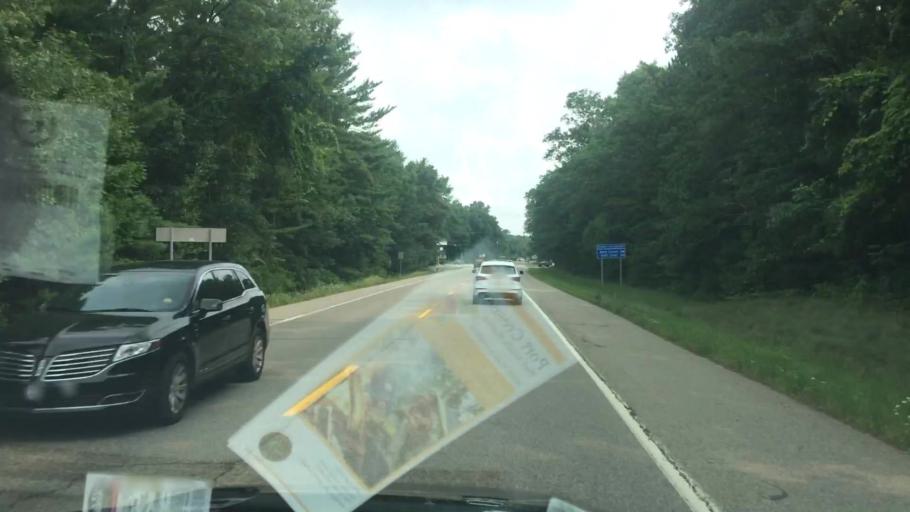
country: US
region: Michigan
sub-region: Huron County
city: Bad Axe
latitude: 44.0005
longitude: -83.0564
